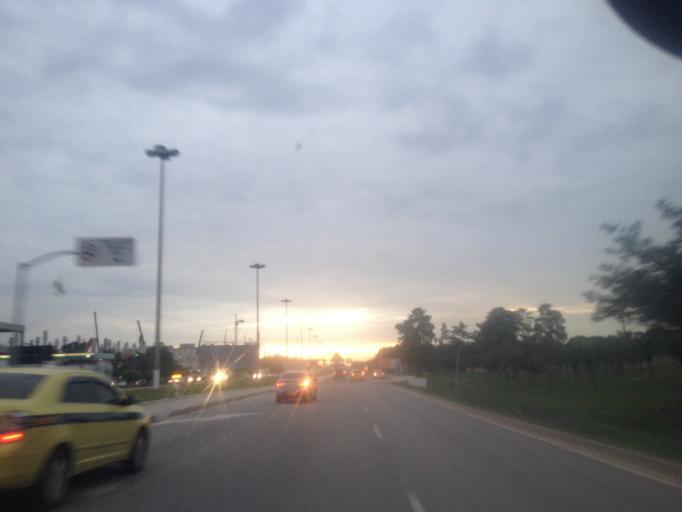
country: BR
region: Rio de Janeiro
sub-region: Duque De Caxias
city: Duque de Caxias
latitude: -22.8172
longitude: -43.2391
